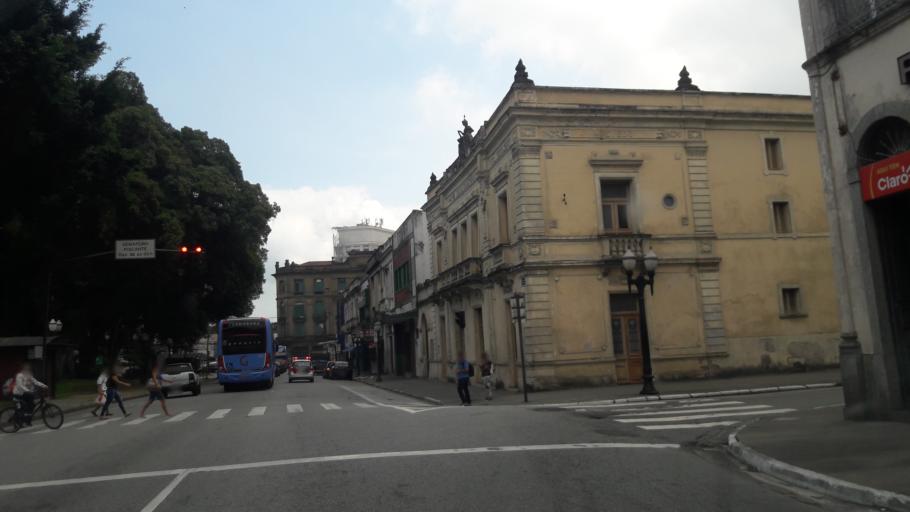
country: BR
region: Sao Paulo
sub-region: Santos
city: Santos
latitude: -23.9354
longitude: -46.3322
